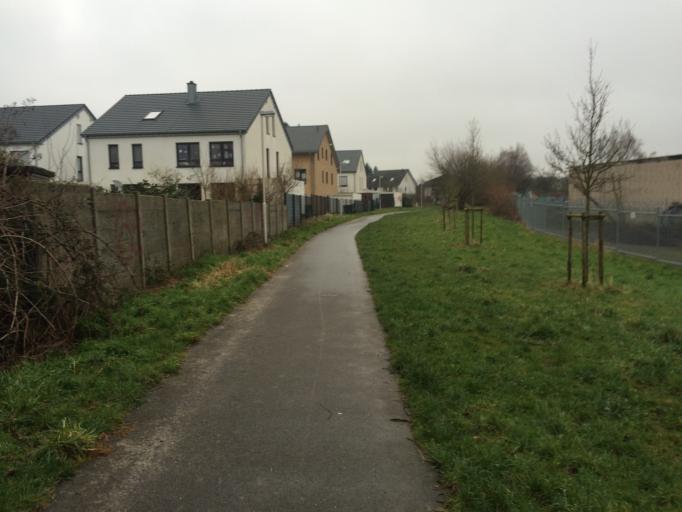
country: NL
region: Limburg
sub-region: Gemeente Kerkrade
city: Kerkrade
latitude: 50.8364
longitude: 6.0820
